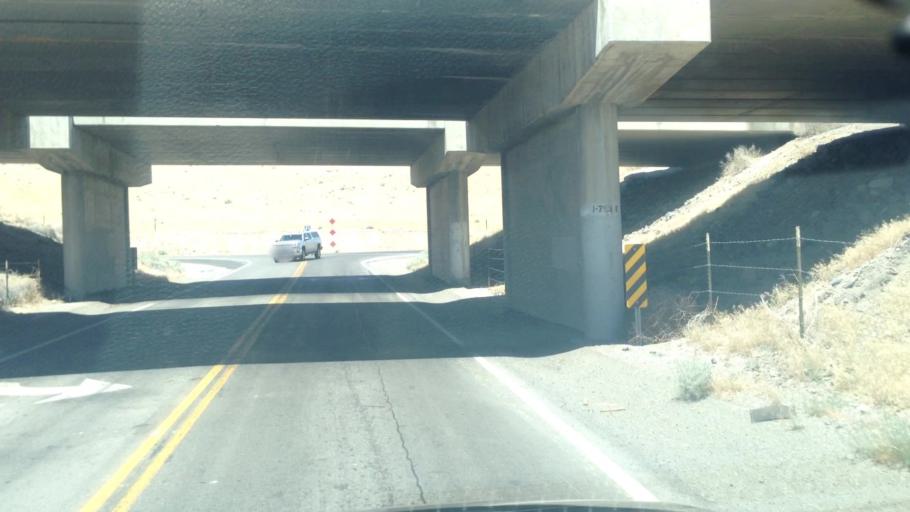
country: US
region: Nevada
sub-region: Washoe County
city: Sparks
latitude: 39.5190
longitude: -119.6295
